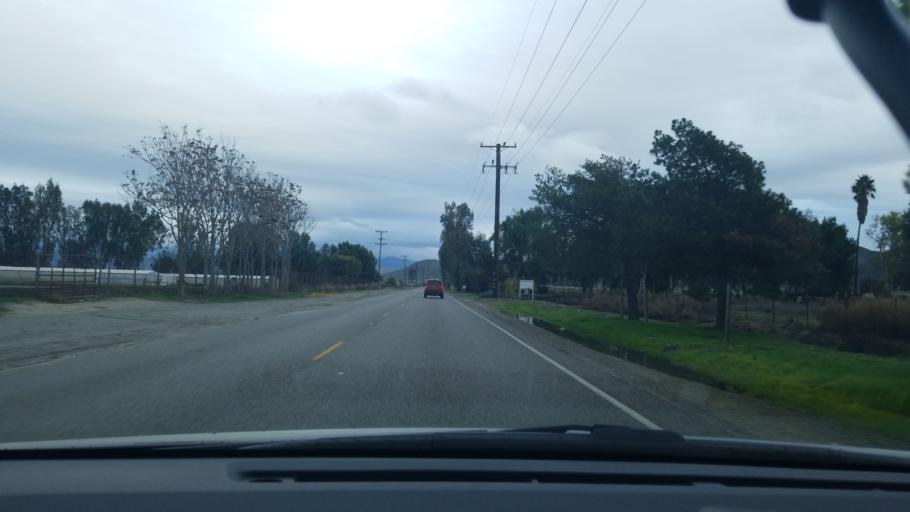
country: US
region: California
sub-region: Riverside County
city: Winchester
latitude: 33.7075
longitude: -117.0521
